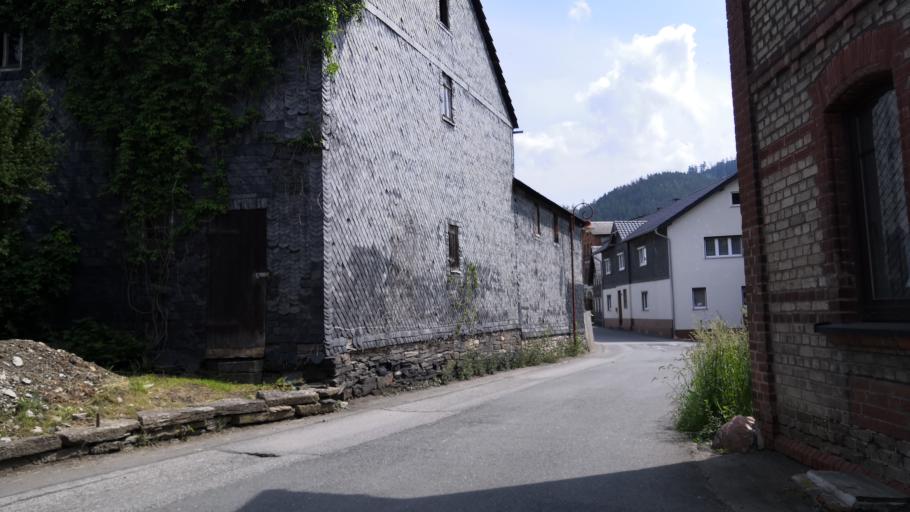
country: DE
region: Thuringia
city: Probstzella
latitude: 50.5651
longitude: 11.3475
